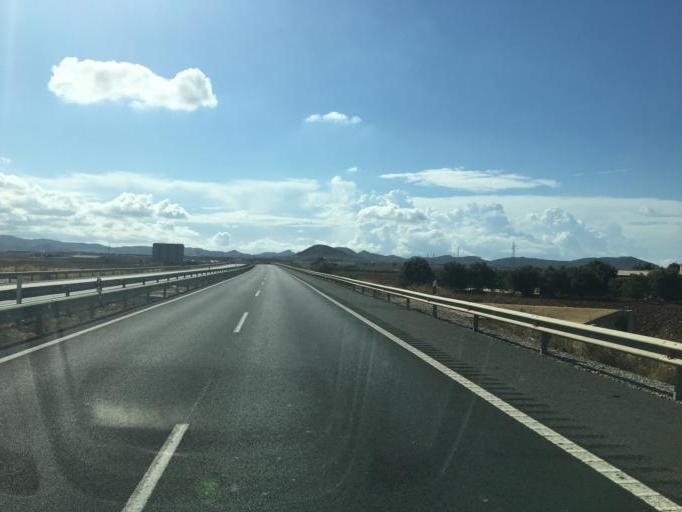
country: ES
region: Murcia
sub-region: Murcia
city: Cartagena
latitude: 37.6516
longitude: -0.9759
